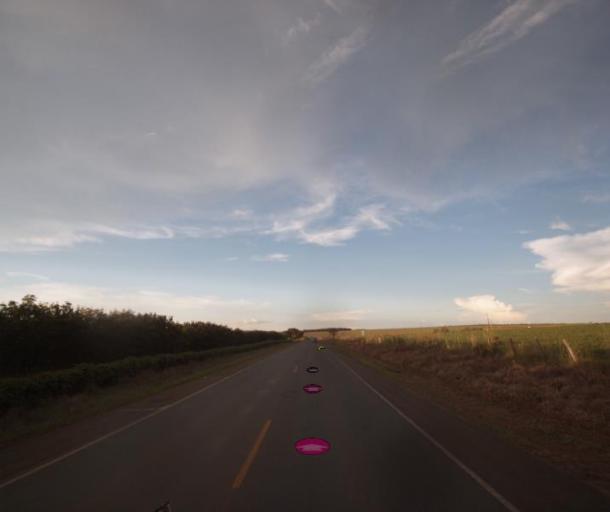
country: BR
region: Goias
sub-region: Anapolis
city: Anapolis
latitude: -16.1890
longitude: -48.9051
